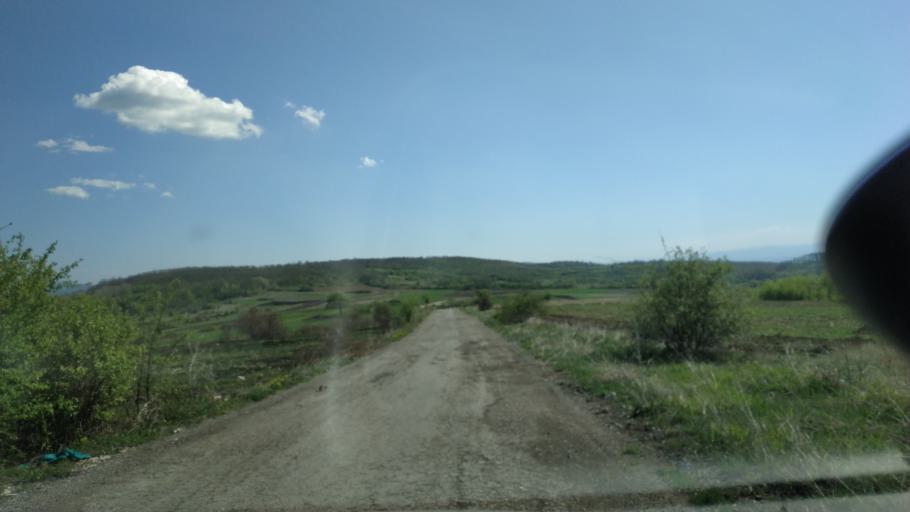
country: RS
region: Central Serbia
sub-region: Zajecarski Okrug
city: Soko Banja
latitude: 43.5190
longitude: 21.9058
